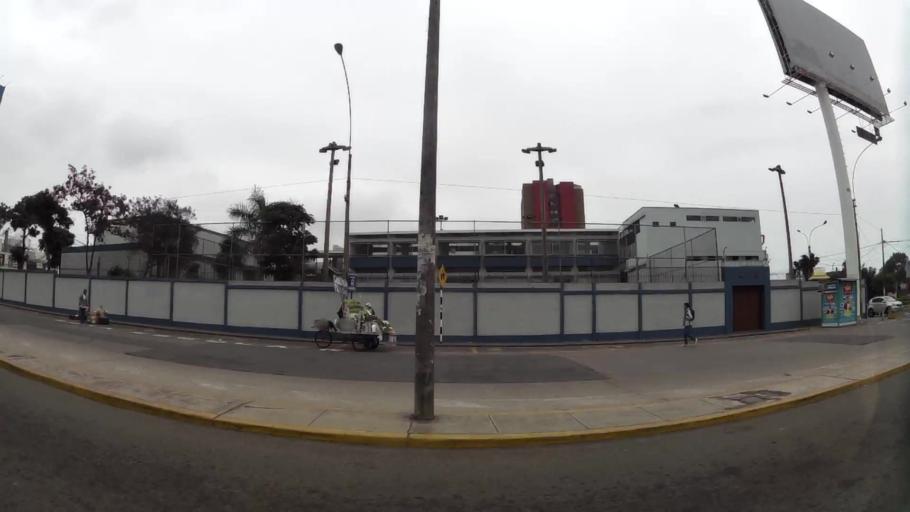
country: PE
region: Lima
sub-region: Lima
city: San Isidro
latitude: -12.1027
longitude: -77.0268
